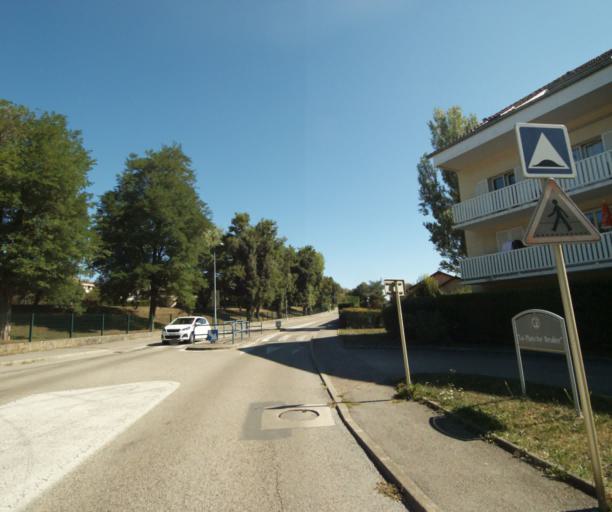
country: FR
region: Rhone-Alpes
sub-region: Departement de l'Ain
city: Ferney-Voltaire
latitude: 46.2534
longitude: 6.0973
